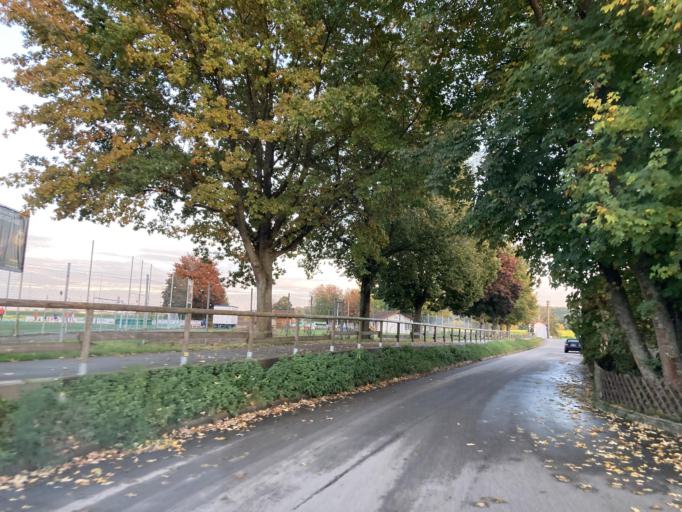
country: DE
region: Baden-Wuerttemberg
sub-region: Regierungsbezirk Stuttgart
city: Bondorf
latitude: 48.4903
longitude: 8.8155
